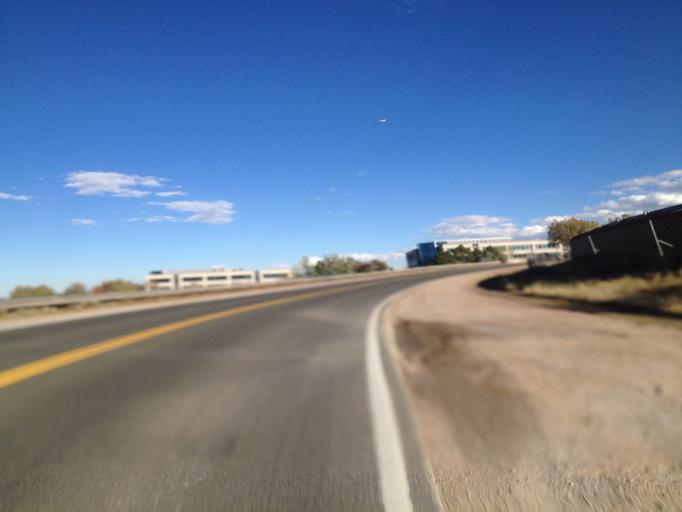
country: US
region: Colorado
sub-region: Broomfield County
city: Broomfield
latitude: 39.9151
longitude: -105.1109
